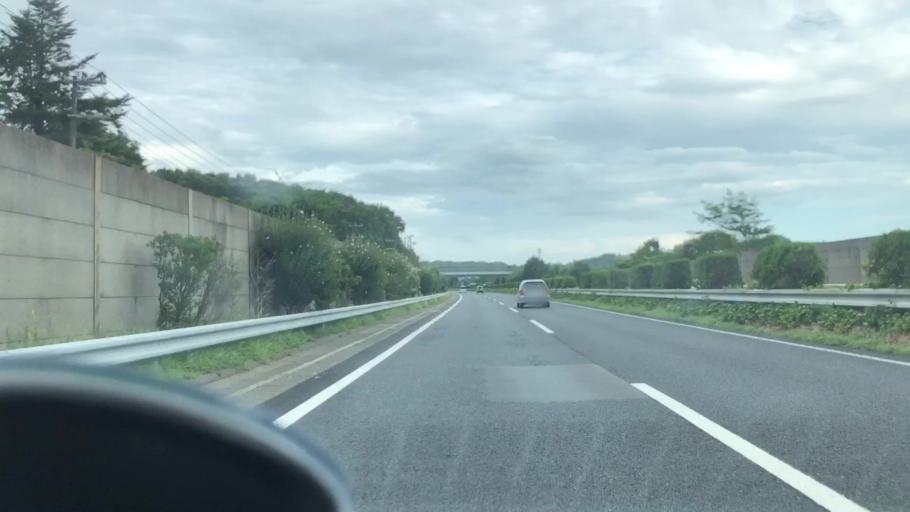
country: JP
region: Hyogo
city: Yashiro
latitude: 34.9238
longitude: 134.9898
